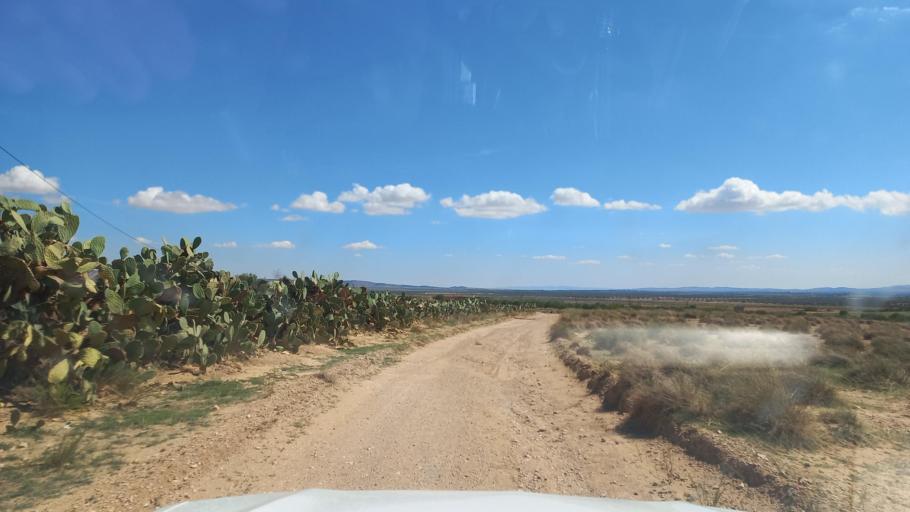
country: TN
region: Al Qasrayn
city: Sbiba
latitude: 35.3530
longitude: 9.0140
